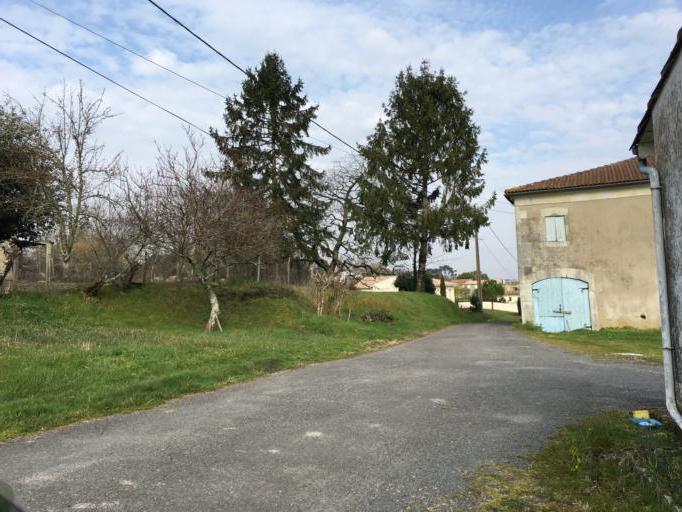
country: FR
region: Aquitaine
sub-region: Departement de la Gironde
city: Saint-Ciers-sur-Gironde
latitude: 45.3285
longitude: -0.5919
